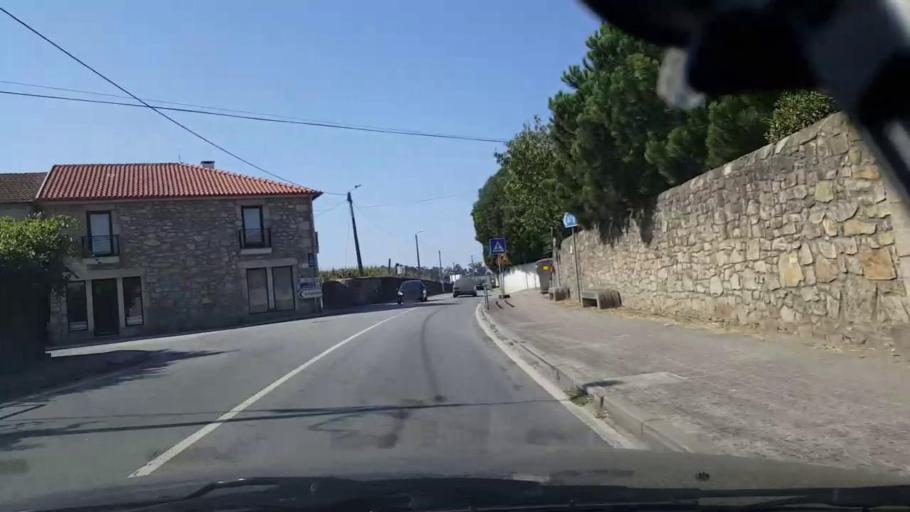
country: PT
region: Porto
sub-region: Povoa de Varzim
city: Pedroso
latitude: 41.3938
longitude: -8.6916
